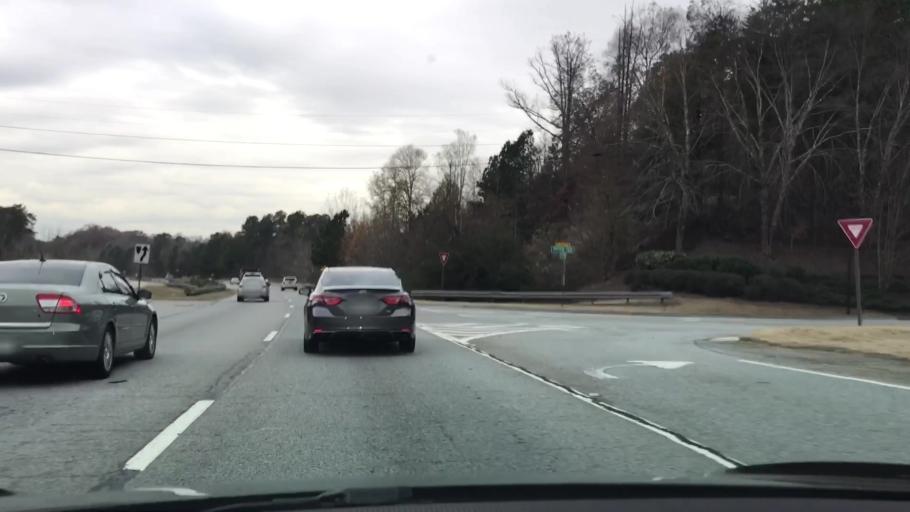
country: US
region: Georgia
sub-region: Gwinnett County
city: Suwanee
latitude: 34.0342
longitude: -84.1058
